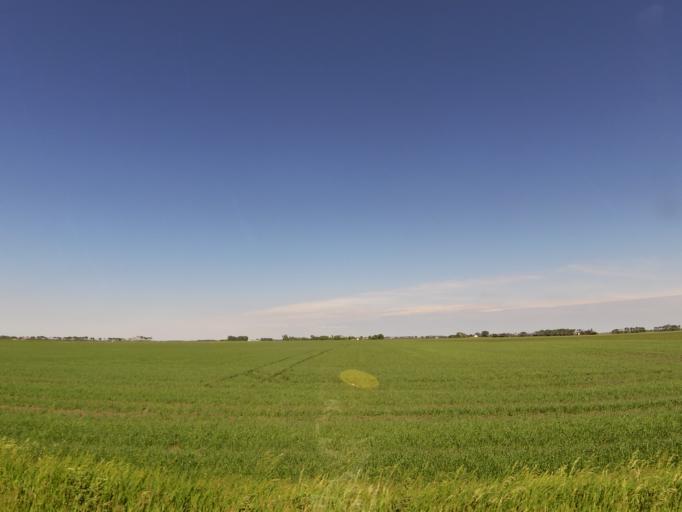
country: US
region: North Dakota
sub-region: Walsh County
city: Grafton
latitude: 48.3501
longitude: -97.2558
